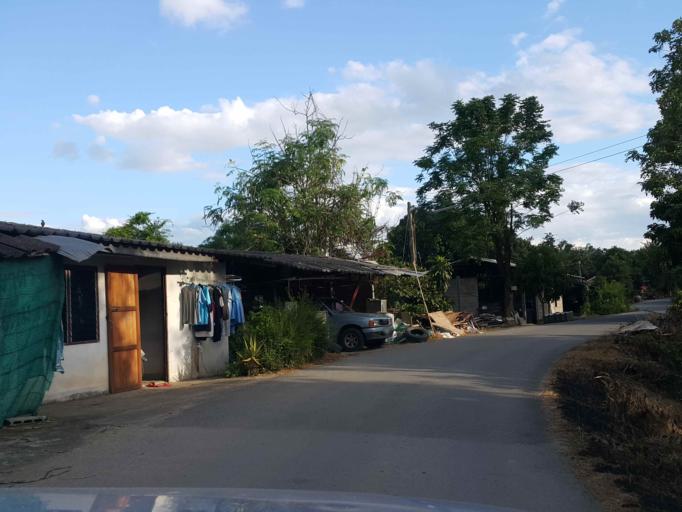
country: TH
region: Chiang Mai
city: San Sai
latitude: 18.9067
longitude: 98.9790
